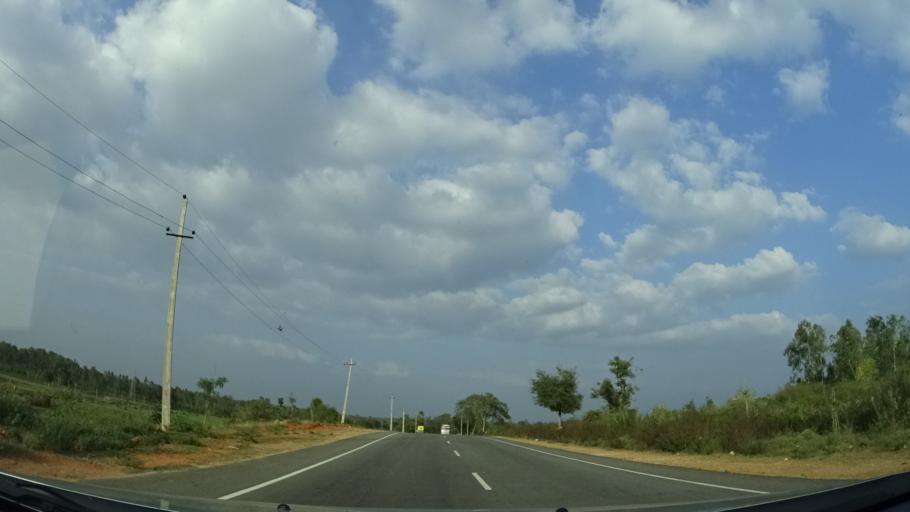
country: IN
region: Karnataka
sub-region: Mandya
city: Malavalli
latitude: 12.3628
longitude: 76.9901
